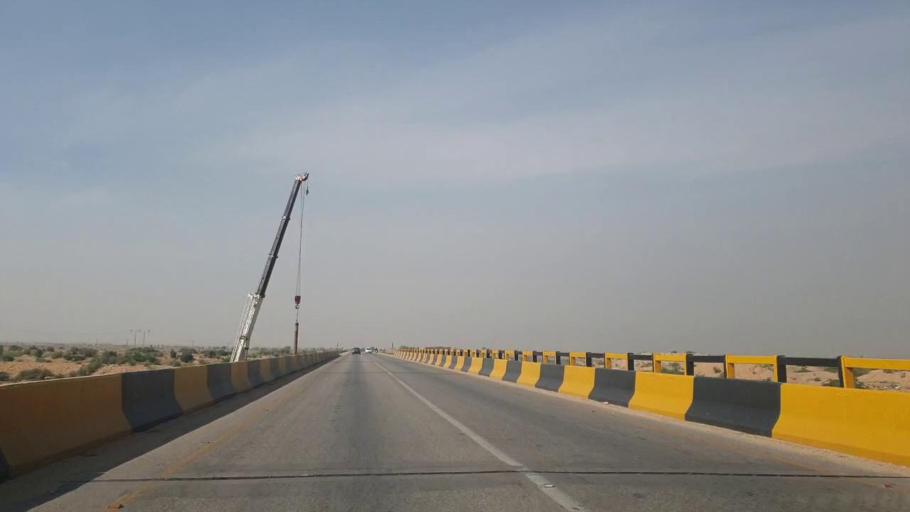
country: PK
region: Sindh
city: Sann
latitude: 26.0365
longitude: 68.1168
